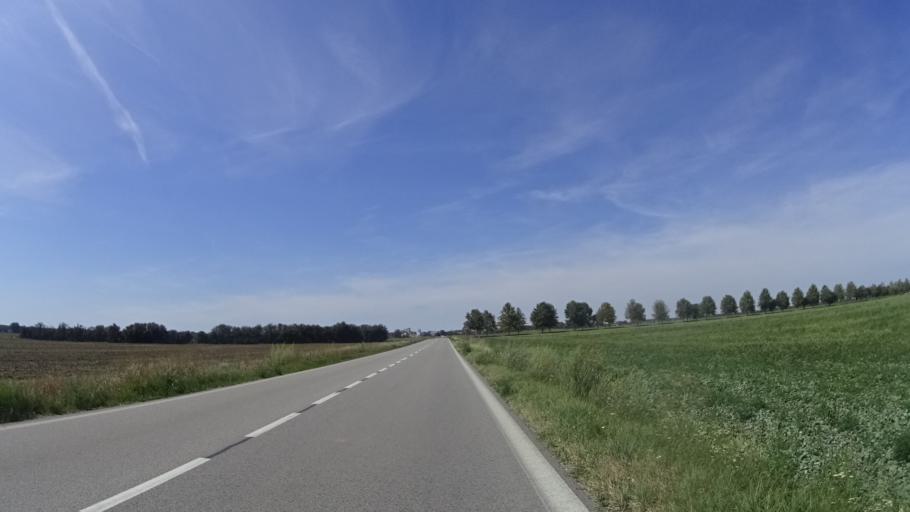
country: AT
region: Lower Austria
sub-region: Politischer Bezirk Ganserndorf
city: Marchegg
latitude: 48.3076
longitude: 16.9387
